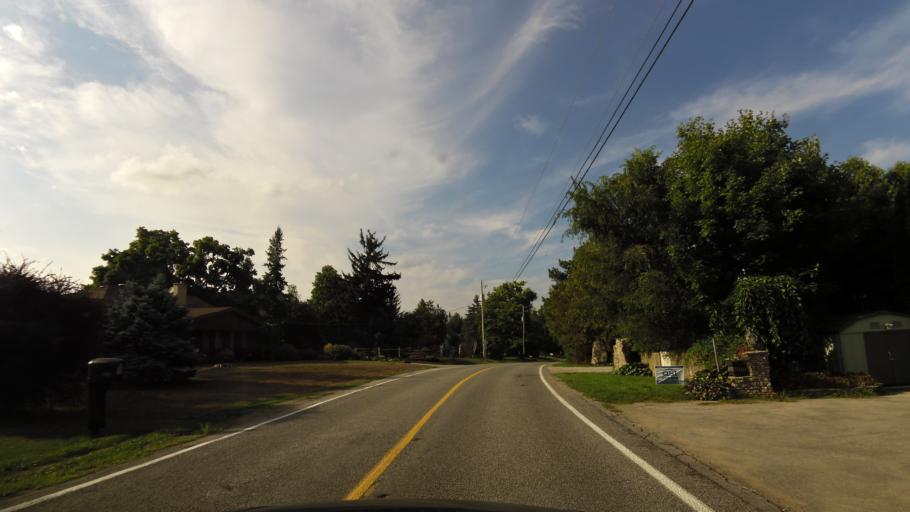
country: CA
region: Ontario
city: Burlington
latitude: 43.3893
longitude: -79.8613
